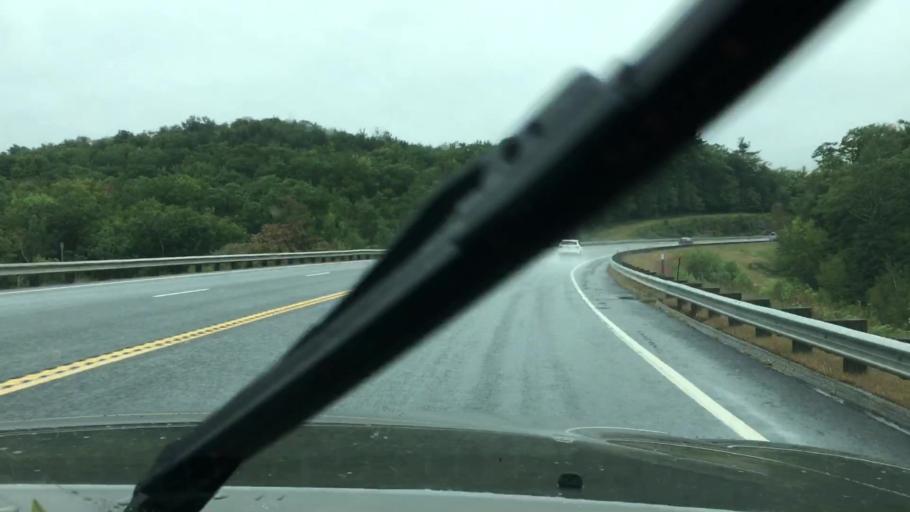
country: US
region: New Hampshire
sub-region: Cheshire County
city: Harrisville
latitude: 43.0096
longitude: -72.1425
